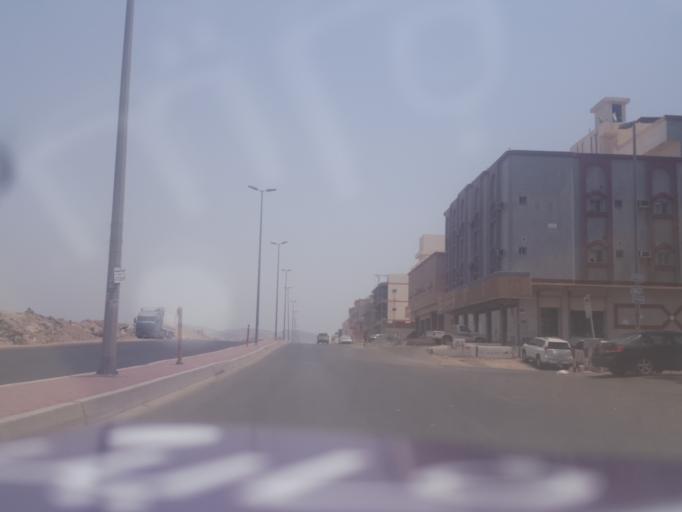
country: SA
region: Makkah
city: Jeddah
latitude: 21.4040
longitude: 39.2715
